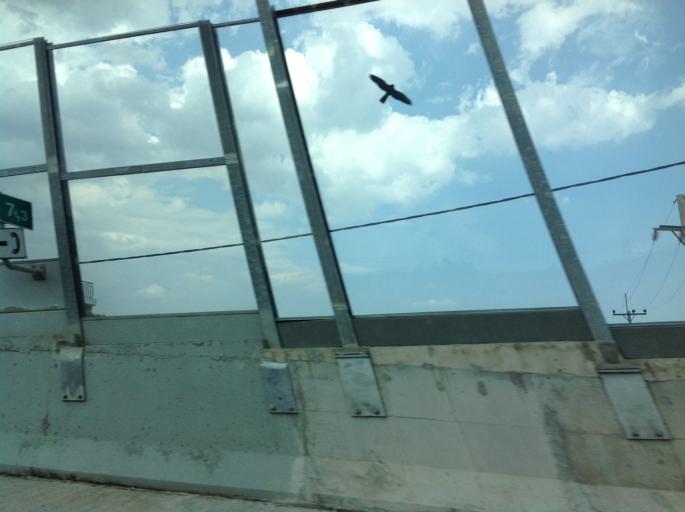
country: GR
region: Attica
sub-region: Nomarchia Anatolikis Attikis
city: Leondarion
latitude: 37.9990
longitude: 23.8440
